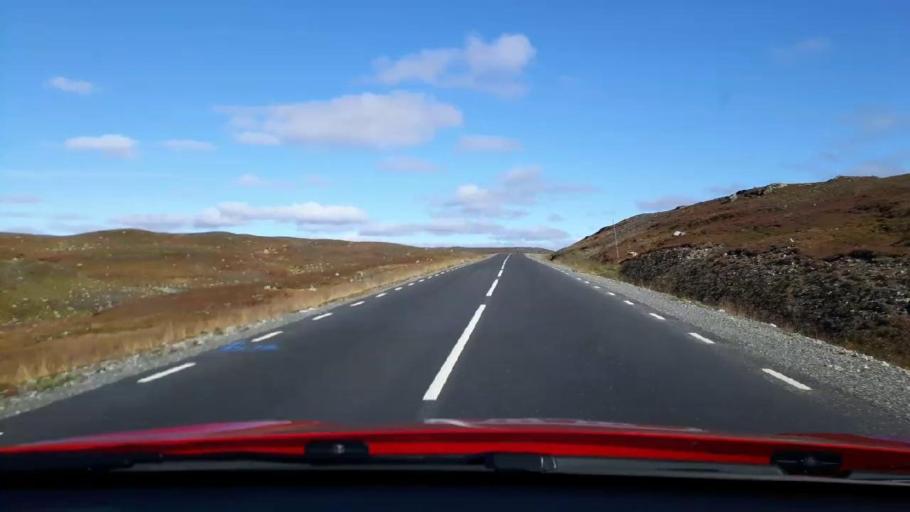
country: NO
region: Nordland
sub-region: Hattfjelldal
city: Hattfjelldal
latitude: 65.0514
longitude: 14.3449
